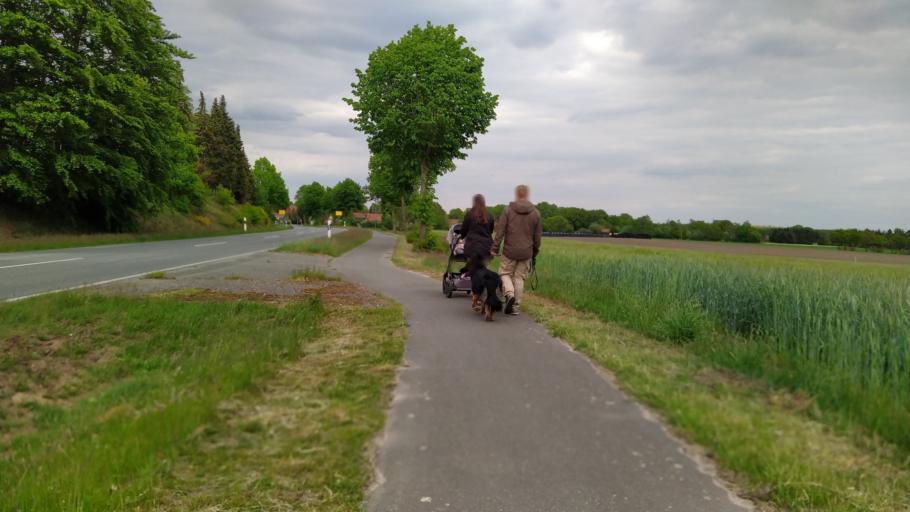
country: DE
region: Lower Saxony
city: Kirchtimke
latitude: 53.2565
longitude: 9.1758
